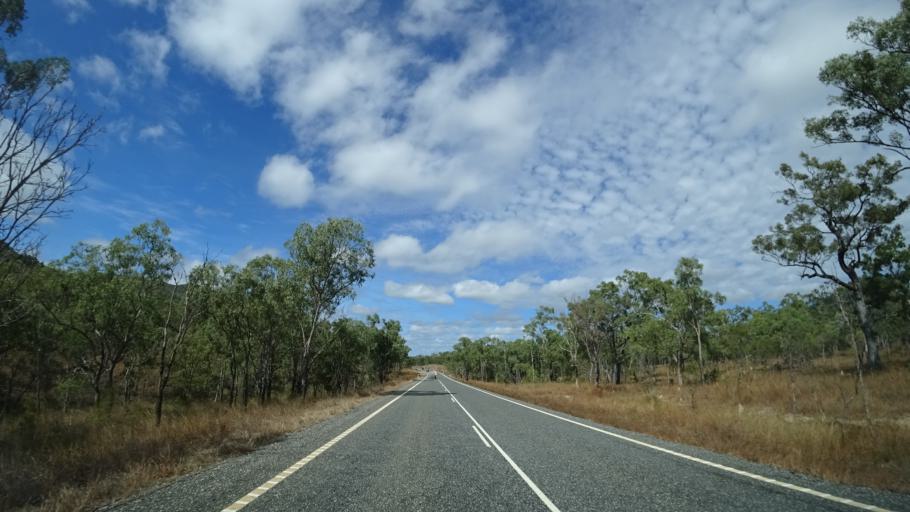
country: AU
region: Queensland
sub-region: Cairns
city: Port Douglas
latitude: -16.3295
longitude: 144.7213
